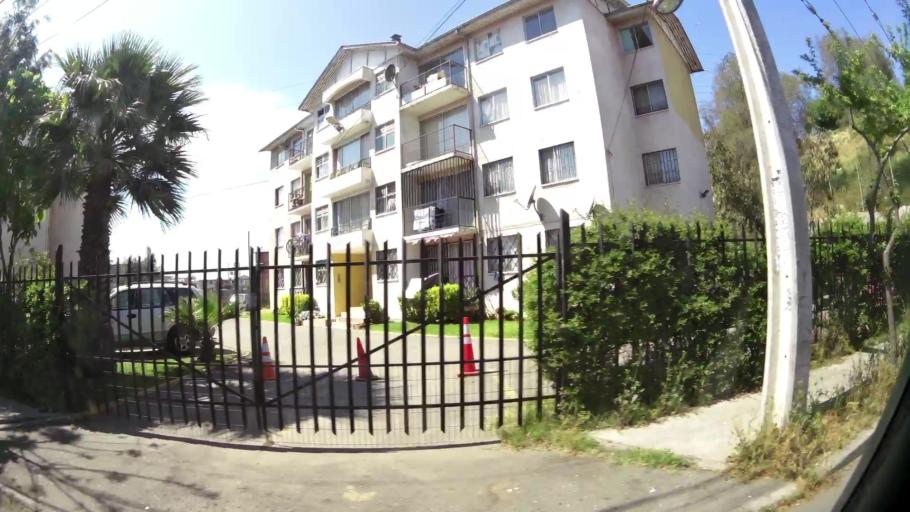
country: CL
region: Santiago Metropolitan
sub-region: Provincia de Santiago
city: Lo Prado
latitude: -33.4866
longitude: -70.7320
